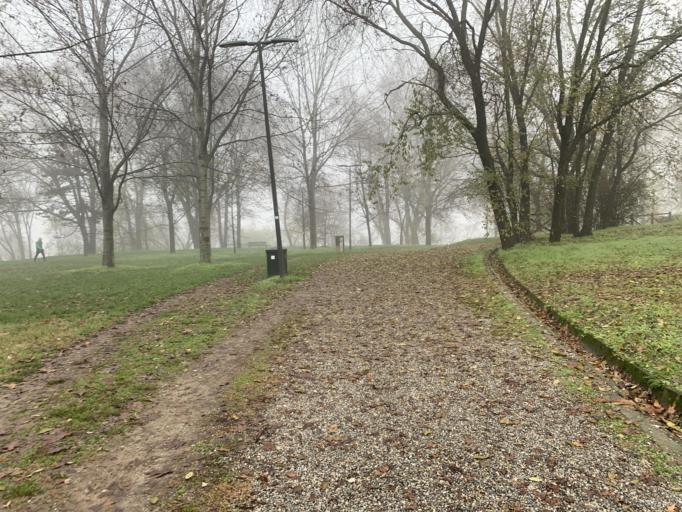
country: IT
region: Lombardy
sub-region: Citta metropolitana di Milano
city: Novate Milanese
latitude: 45.4912
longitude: 9.1341
